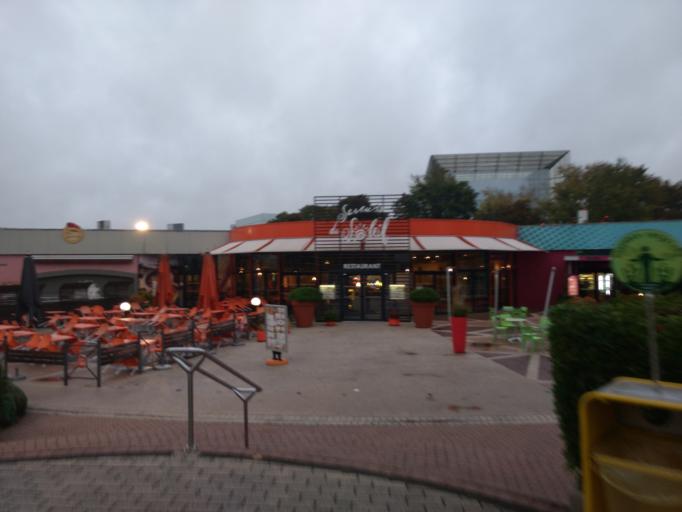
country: FR
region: Poitou-Charentes
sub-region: Departement de la Vienne
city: Jaunay-Clan
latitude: 46.6709
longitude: 0.3701
